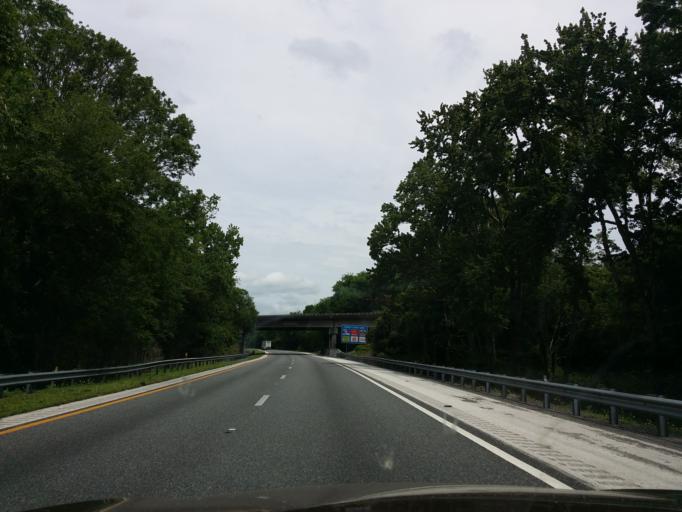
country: US
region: Florida
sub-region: Sumter County
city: Wildwood
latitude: 28.8551
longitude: -82.0900
